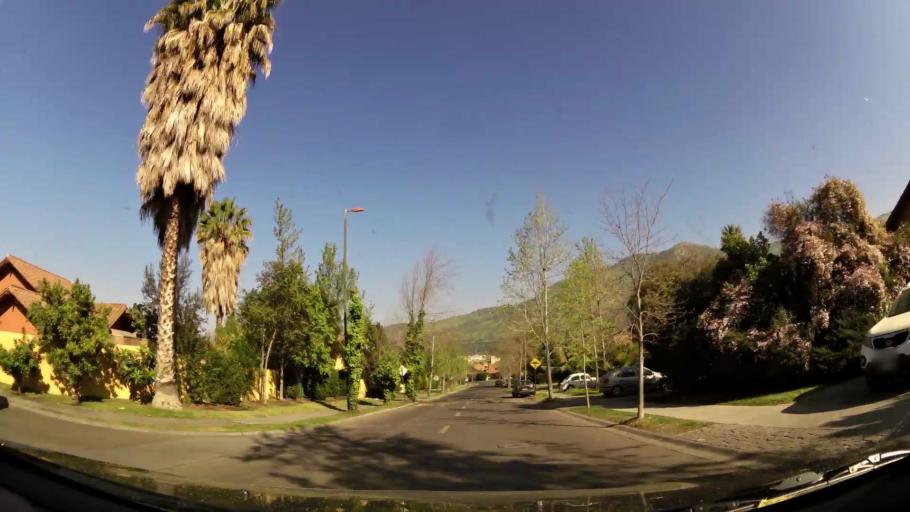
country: CL
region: Santiago Metropolitan
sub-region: Provincia de Chacabuco
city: Chicureo Abajo
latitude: -33.3453
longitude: -70.6658
